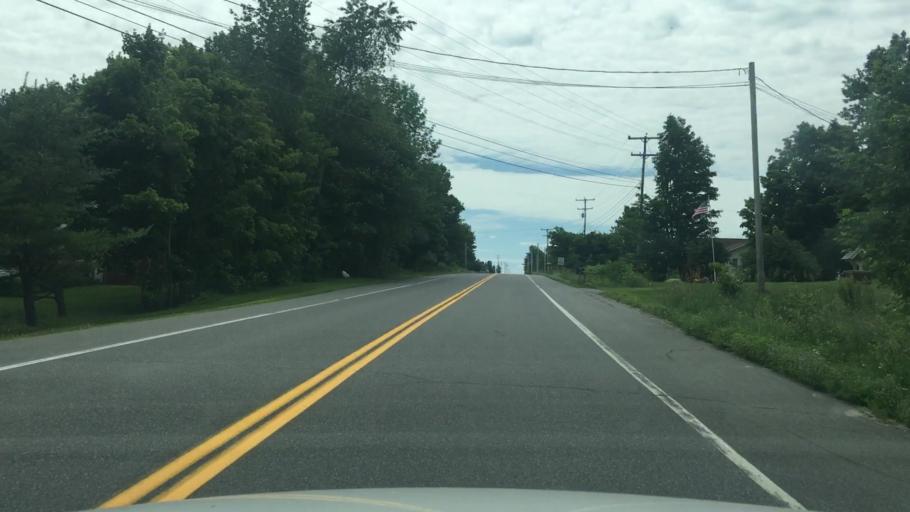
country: US
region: Maine
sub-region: Waldo County
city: Troy
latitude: 44.5608
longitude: -69.2715
